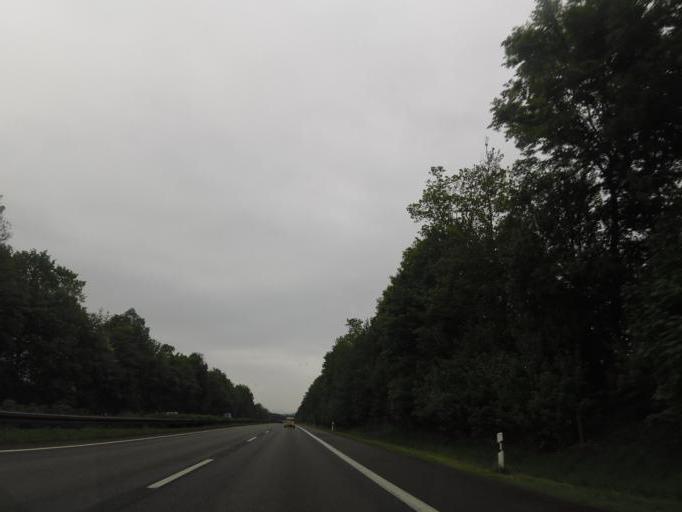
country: DE
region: Lower Saxony
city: Northeim
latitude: 51.7536
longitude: 10.0111
